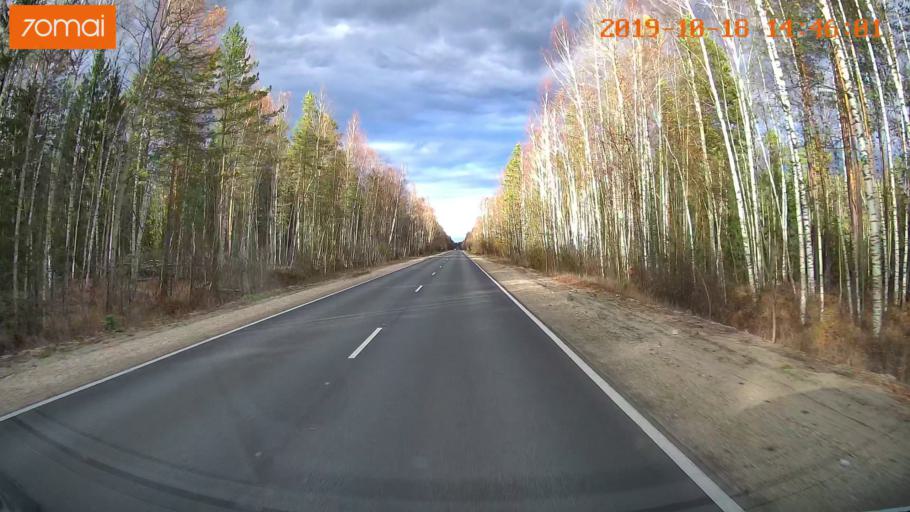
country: RU
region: Vladimir
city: Velikodvorskiy
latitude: 55.3643
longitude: 40.6800
